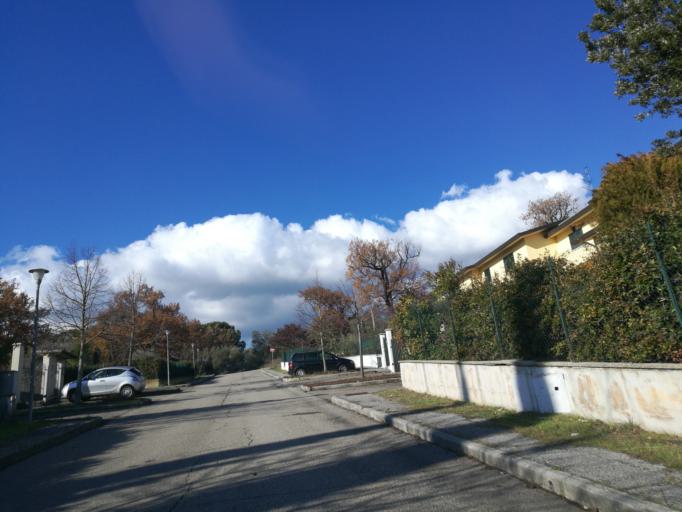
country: IT
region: Umbria
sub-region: Provincia di Perugia
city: Perugia
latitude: 43.0800
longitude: 12.3818
